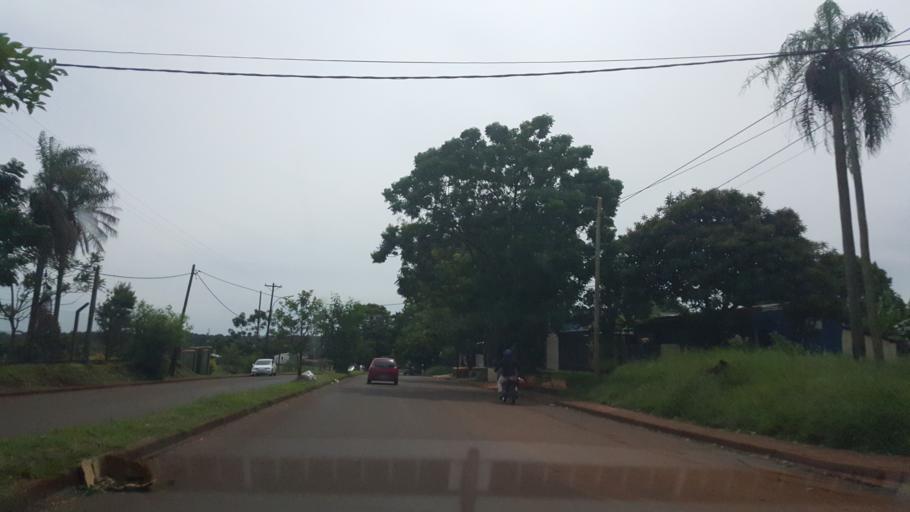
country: AR
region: Misiones
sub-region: Departamento de Capital
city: Posadas
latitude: -27.3949
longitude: -55.9432
